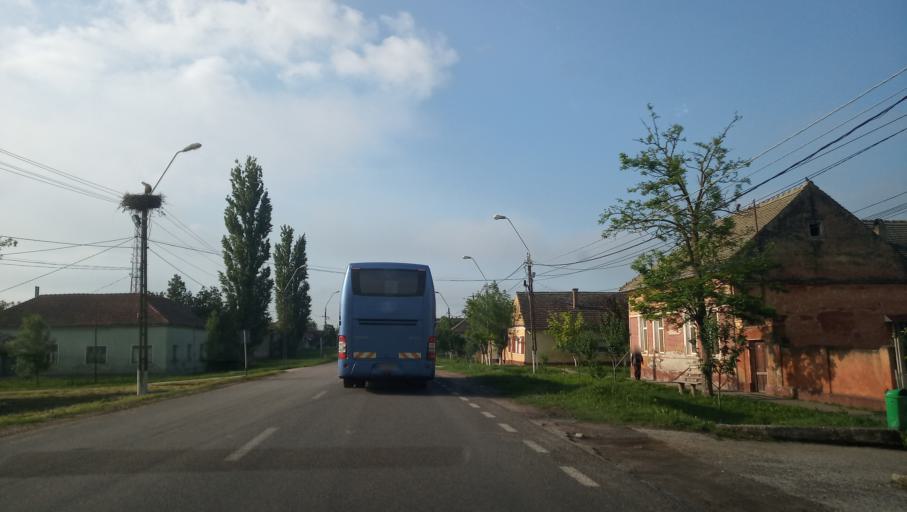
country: RO
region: Timis
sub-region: Comuna Moravita
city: Moravita
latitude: 45.2553
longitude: 21.2672
